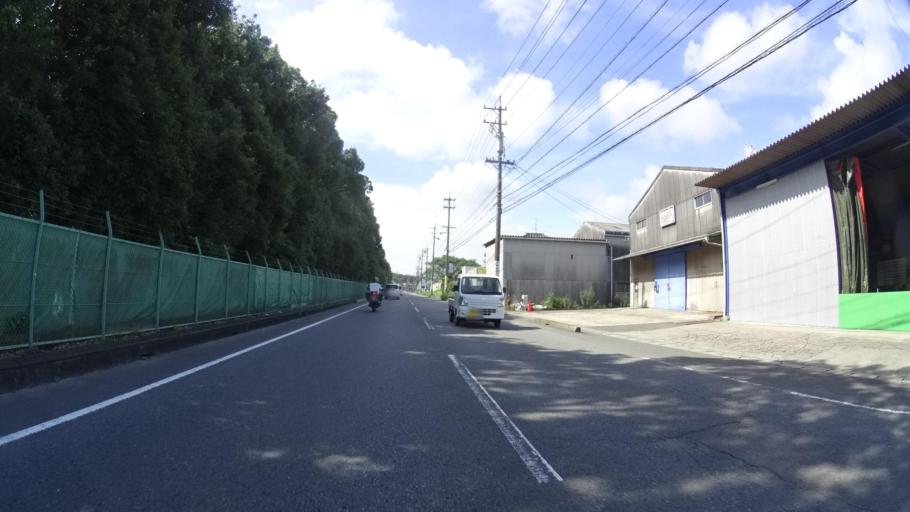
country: JP
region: Mie
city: Kawage
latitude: 34.8617
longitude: 136.5202
